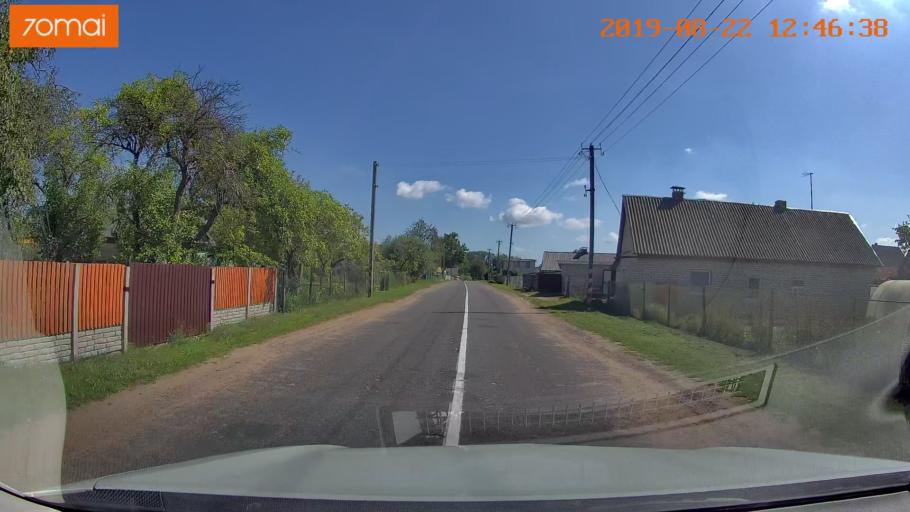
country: BY
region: Minsk
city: Prawdzinski
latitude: 53.4586
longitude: 27.6315
